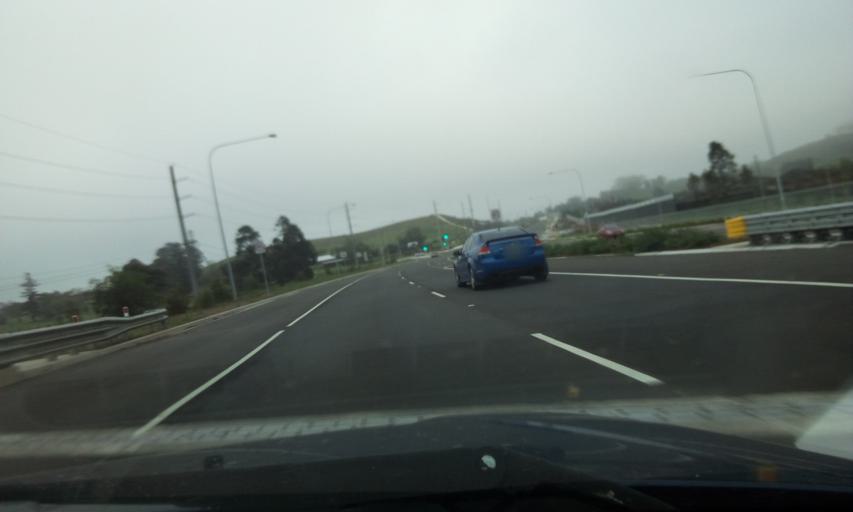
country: AU
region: New South Wales
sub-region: Camden
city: Narellan
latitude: -34.0284
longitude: 150.7271
